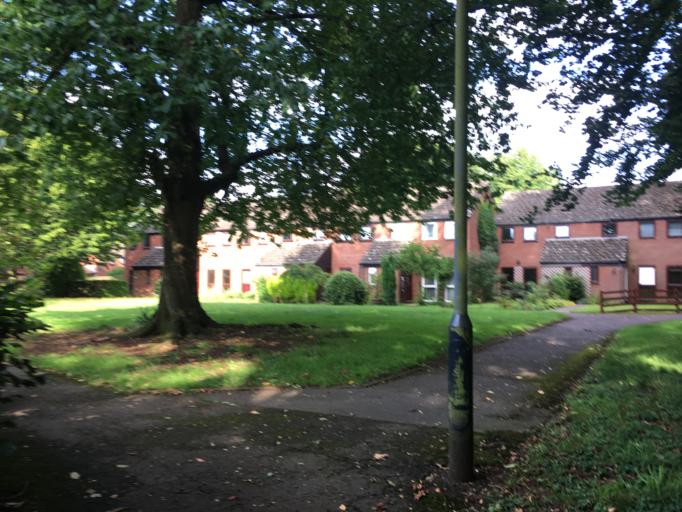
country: GB
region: England
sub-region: Warwickshire
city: Rugby
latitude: 52.3831
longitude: -1.2188
